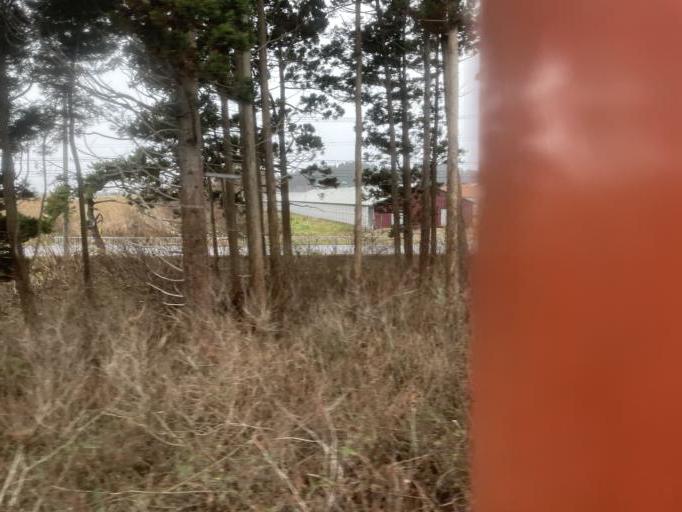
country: JP
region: Aomori
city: Aomori Shi
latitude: 40.9829
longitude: 140.6537
